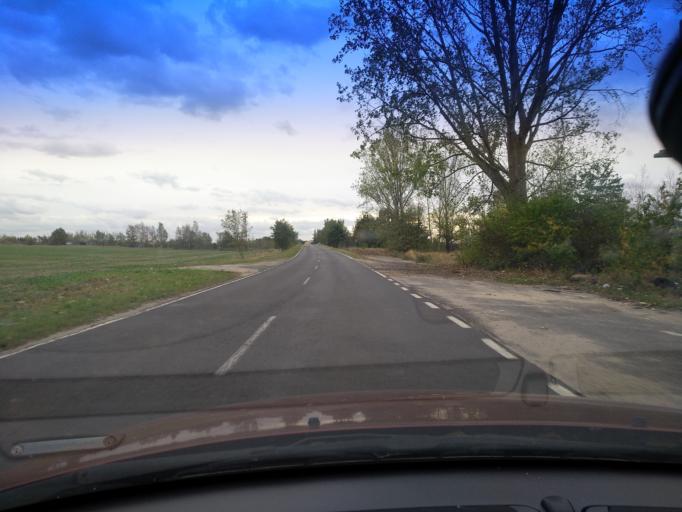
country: PL
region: Lower Silesian Voivodeship
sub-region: Powiat zgorzelecki
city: Zgorzelec
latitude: 51.1818
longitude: 15.0141
